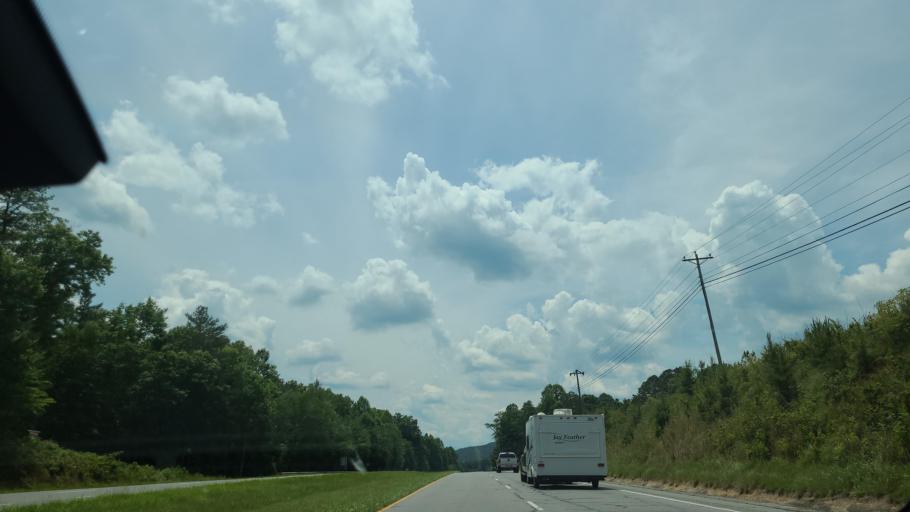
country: US
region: North Carolina
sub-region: Cherokee County
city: Murphy
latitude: 35.0205
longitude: -84.1761
